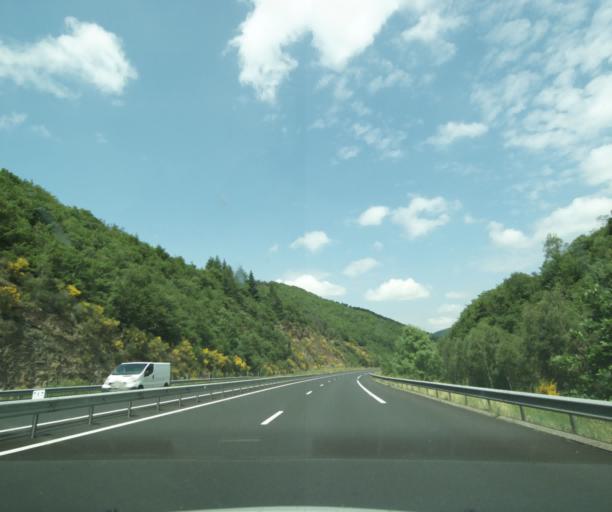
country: FR
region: Auvergne
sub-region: Departement du Cantal
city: Massiac
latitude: 45.2143
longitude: 3.2009
